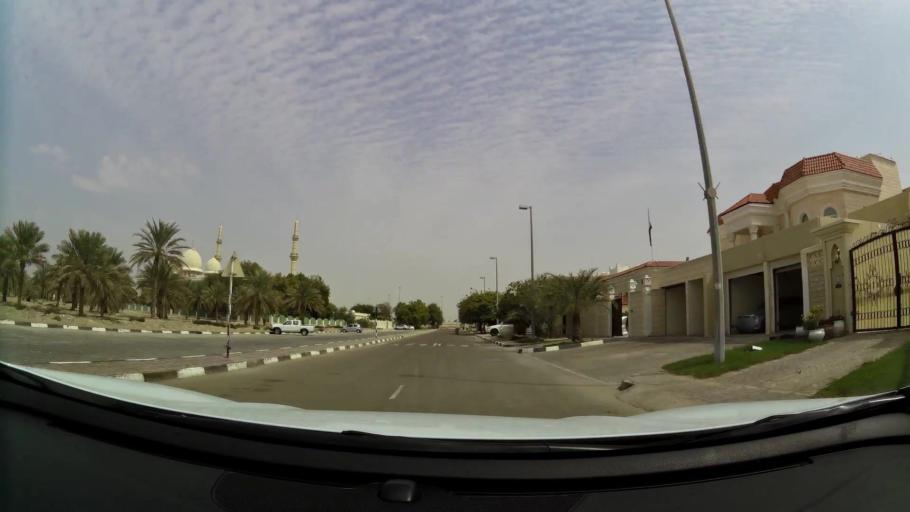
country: AE
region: Abu Dhabi
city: Abu Dhabi
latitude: 24.5406
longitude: 54.6897
